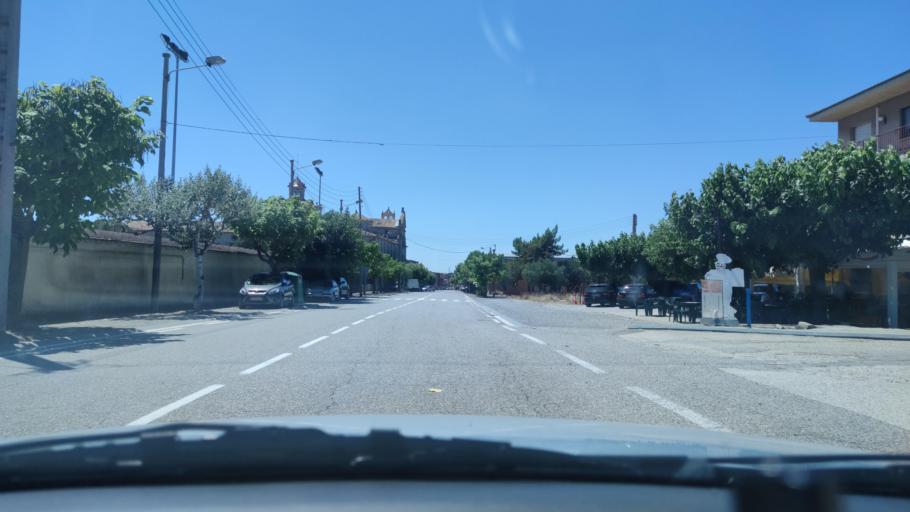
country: ES
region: Catalonia
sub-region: Provincia de Lleida
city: Ivorra
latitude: 41.7264
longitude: 1.3713
